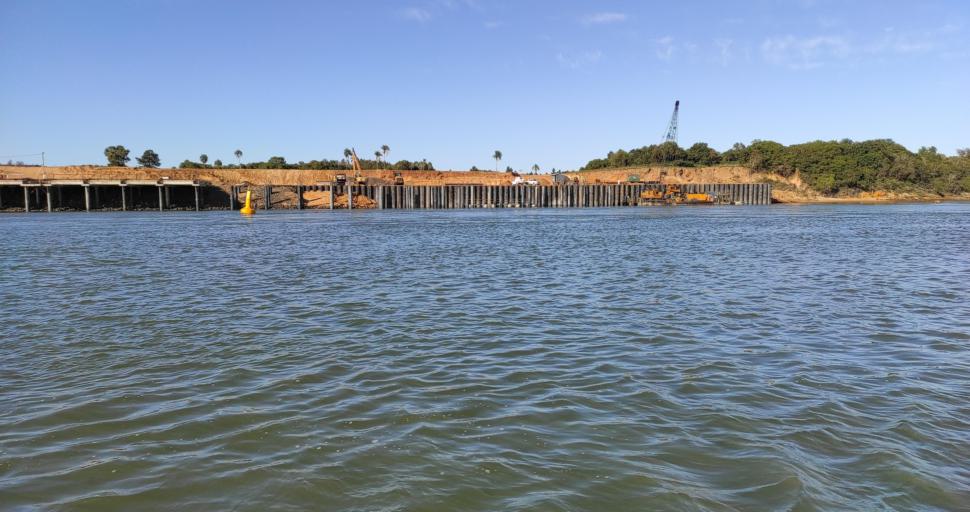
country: AR
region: Corrientes
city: Ituzaingo
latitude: -27.6064
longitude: -56.8360
